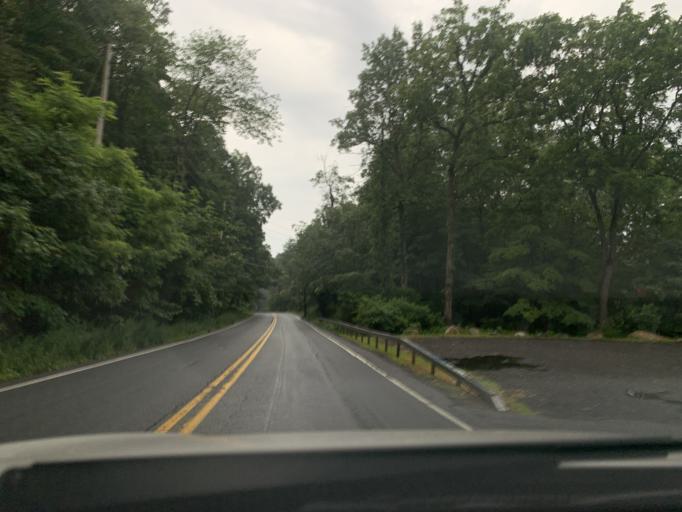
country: US
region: New York
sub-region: Westchester County
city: Ossining
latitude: 41.1902
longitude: -73.8403
